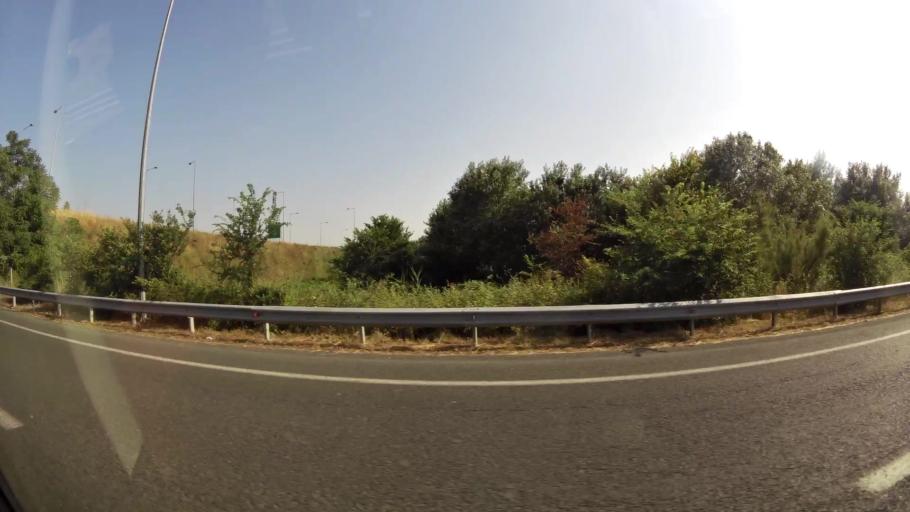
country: GR
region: Central Macedonia
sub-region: Nomos Imathias
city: Agkathia
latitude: 40.5874
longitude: 22.4717
